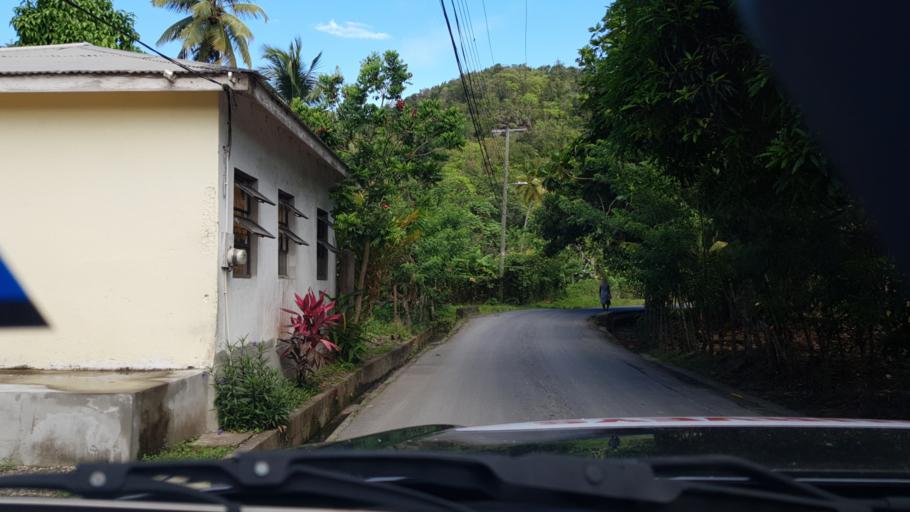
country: LC
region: Anse-la-Raye
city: Anse La Raye
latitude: 13.9386
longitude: -61.0413
